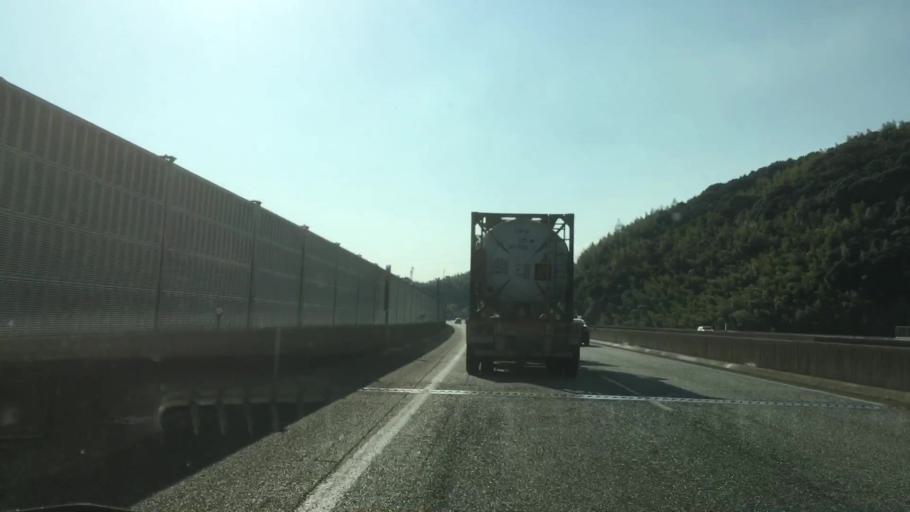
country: JP
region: Yamaguchi
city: Kudamatsu
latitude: 34.0443
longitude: 131.8682
